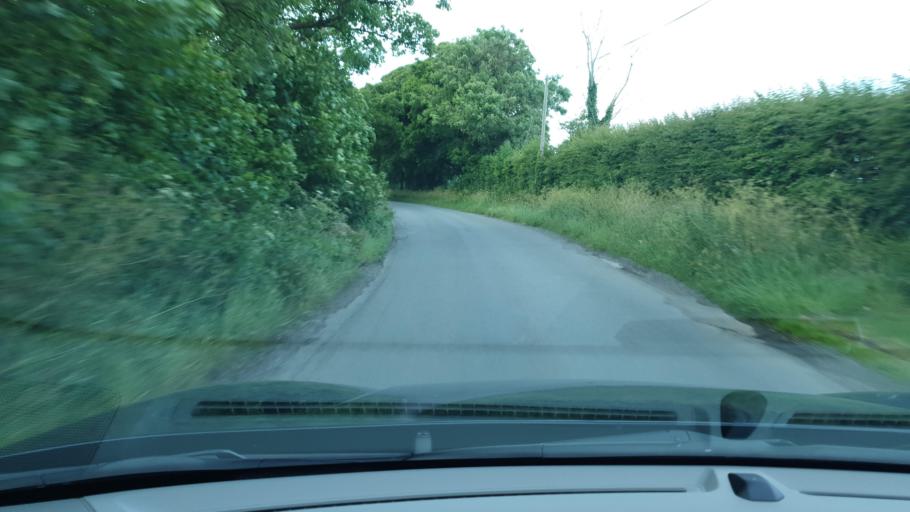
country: IE
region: Leinster
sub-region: An Mhi
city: Ratoath
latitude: 53.5601
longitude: -6.4969
